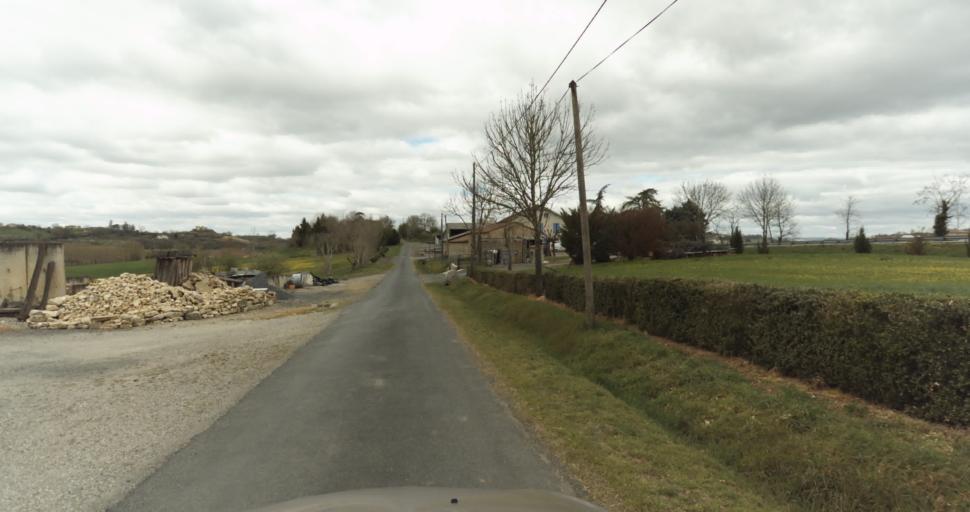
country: FR
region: Midi-Pyrenees
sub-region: Departement du Tarn
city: Puygouzon
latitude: 43.8714
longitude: 2.1810
